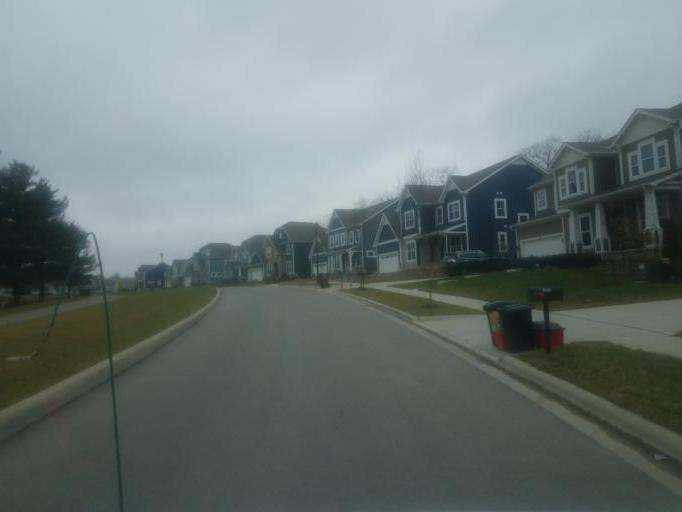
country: US
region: Ohio
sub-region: Franklin County
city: Westerville
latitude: 40.1318
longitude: -82.9526
